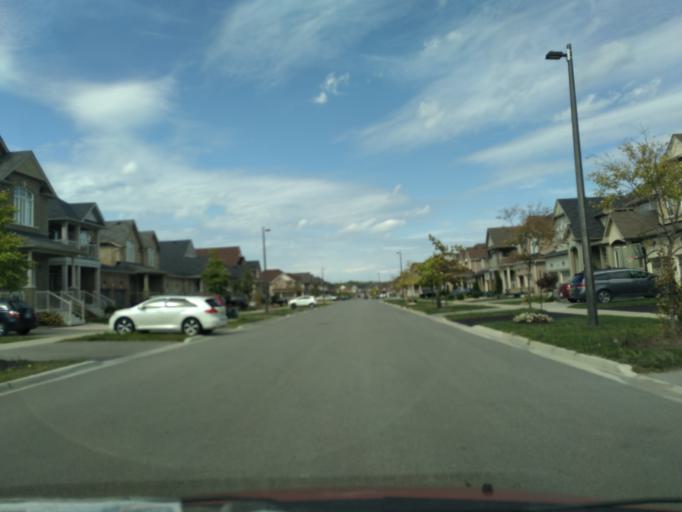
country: CA
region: Ontario
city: Keswick
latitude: 44.3029
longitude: -79.3766
